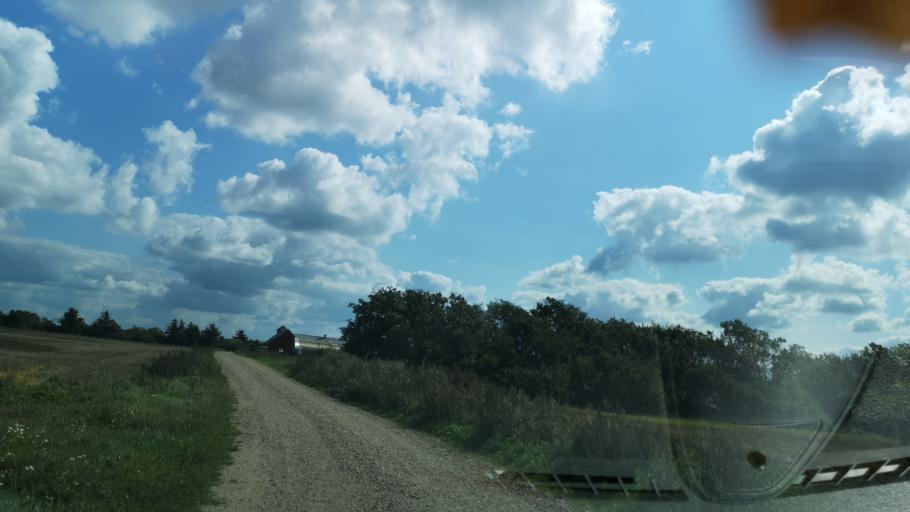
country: DK
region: Central Jutland
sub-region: Ringkobing-Skjern Kommune
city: Skjern
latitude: 55.9043
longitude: 8.3963
